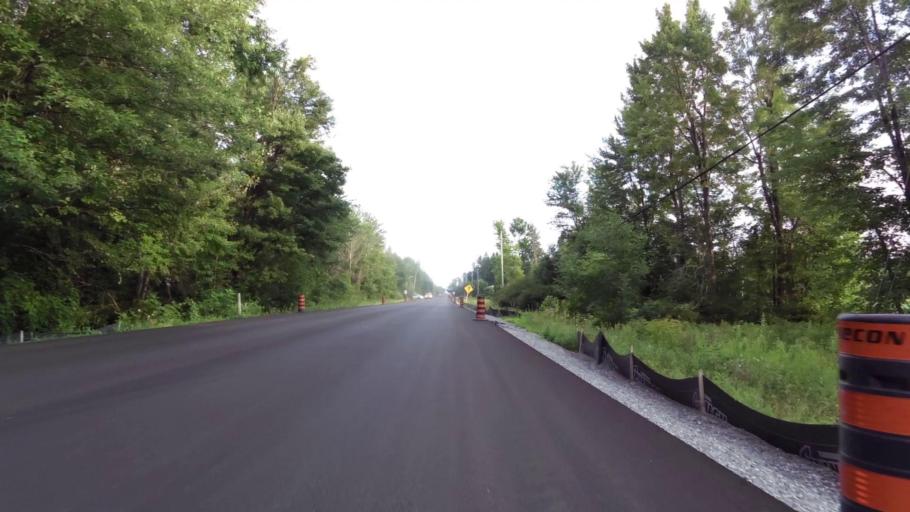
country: CA
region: Ontario
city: Ottawa
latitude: 45.2608
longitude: -75.5966
